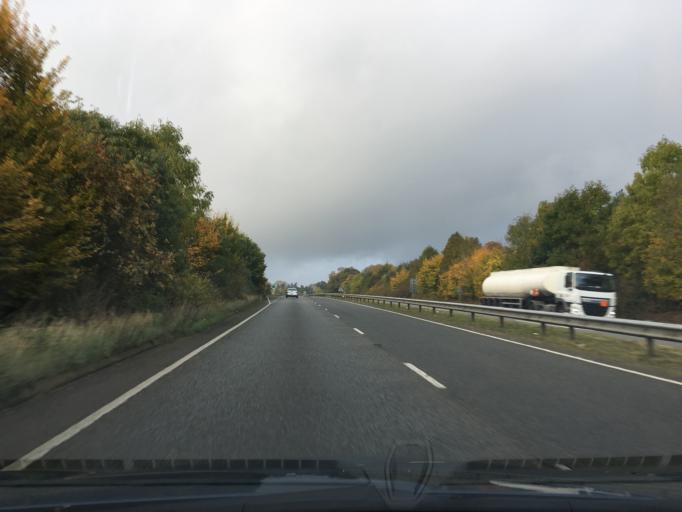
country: GB
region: England
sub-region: Hampshire
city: Kingsley
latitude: 51.1918
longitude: -0.8582
